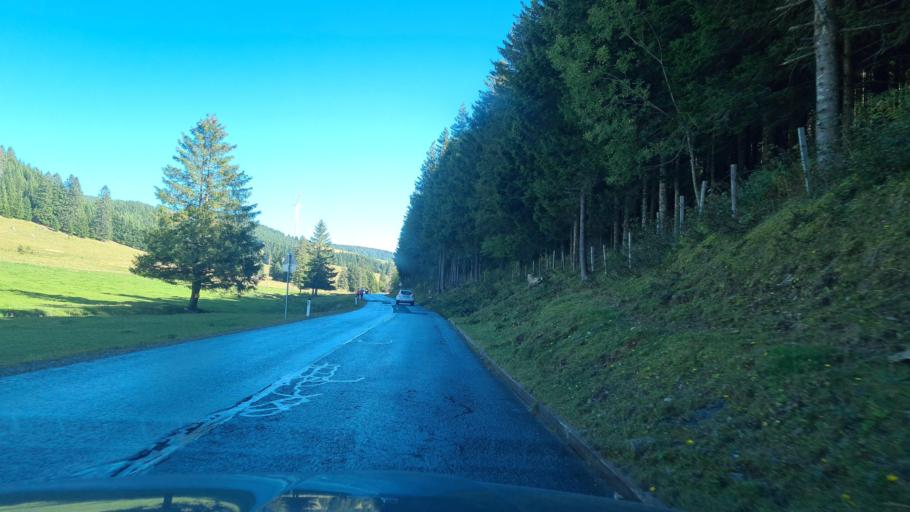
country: AT
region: Styria
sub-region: Politischer Bezirk Weiz
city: Gasen
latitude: 47.3511
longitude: 15.5227
